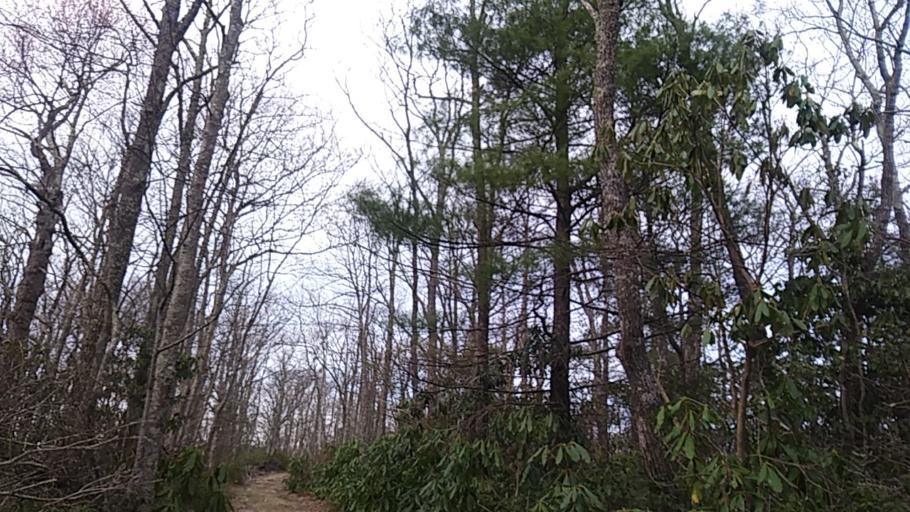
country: US
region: Tennessee
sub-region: Greene County
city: Tusculum
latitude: 36.0604
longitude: -82.6760
